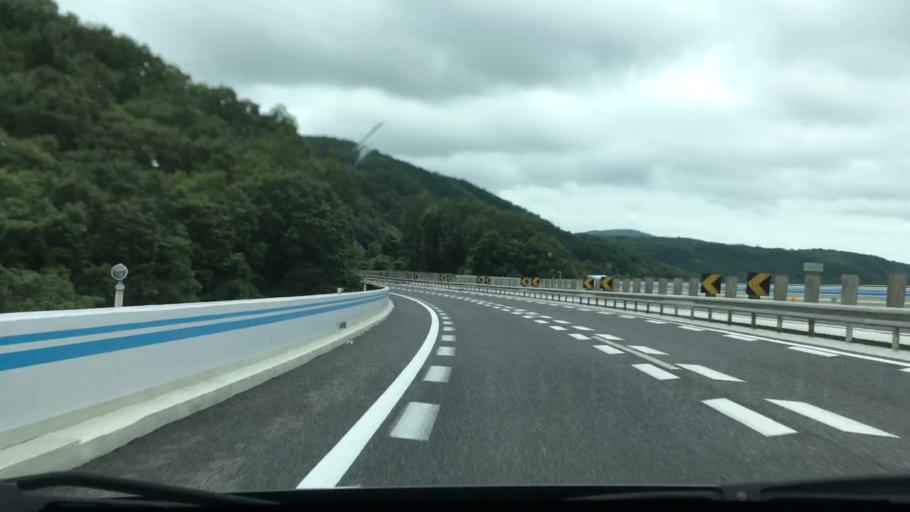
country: JP
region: Hiroshima
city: Miyoshi
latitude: 34.7840
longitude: 132.8443
